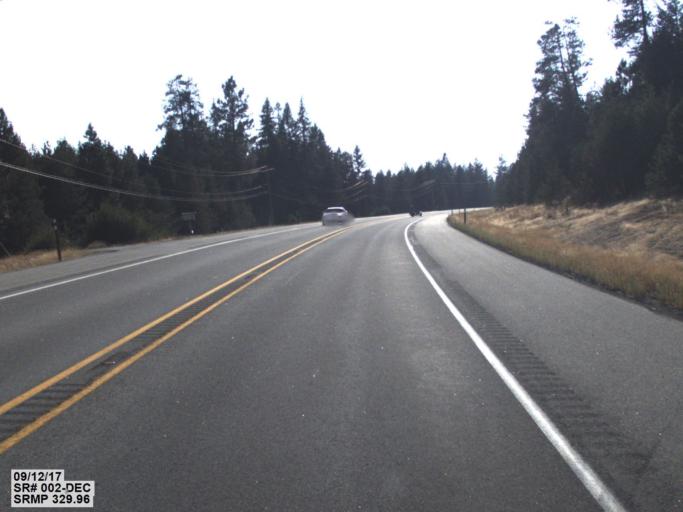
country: US
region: Washington
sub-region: Pend Oreille County
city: Newport
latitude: 48.1500
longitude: -117.1150
